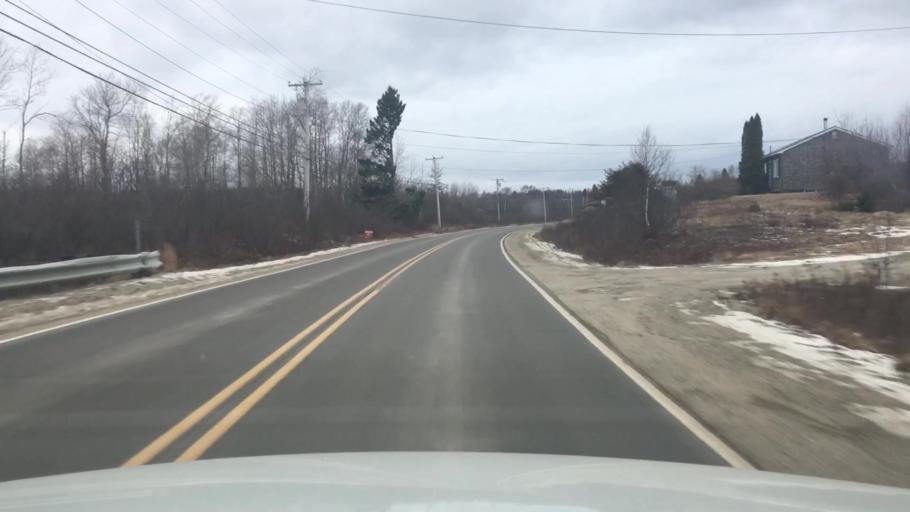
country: US
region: Maine
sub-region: Washington County
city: Jonesport
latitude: 44.5533
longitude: -67.6247
